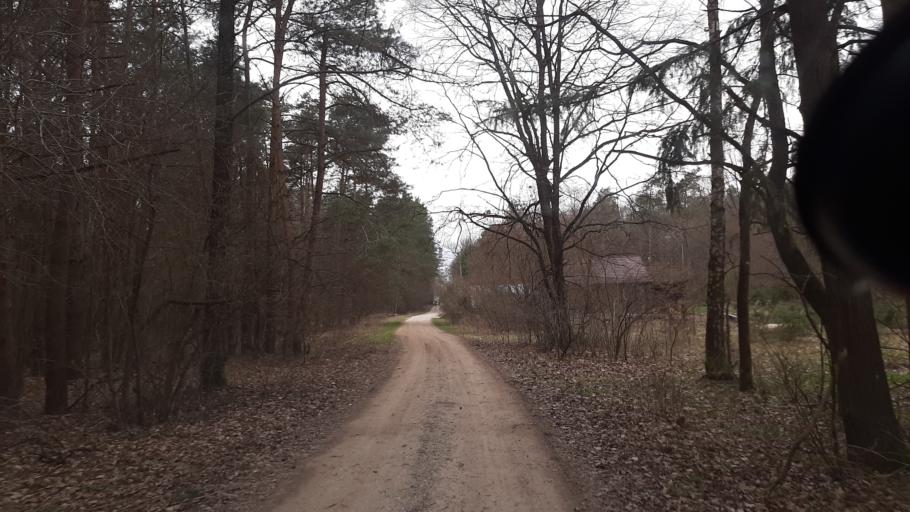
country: PL
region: Lublin Voivodeship
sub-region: Powiat lubartowski
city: Abramow
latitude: 51.4447
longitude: 22.3407
